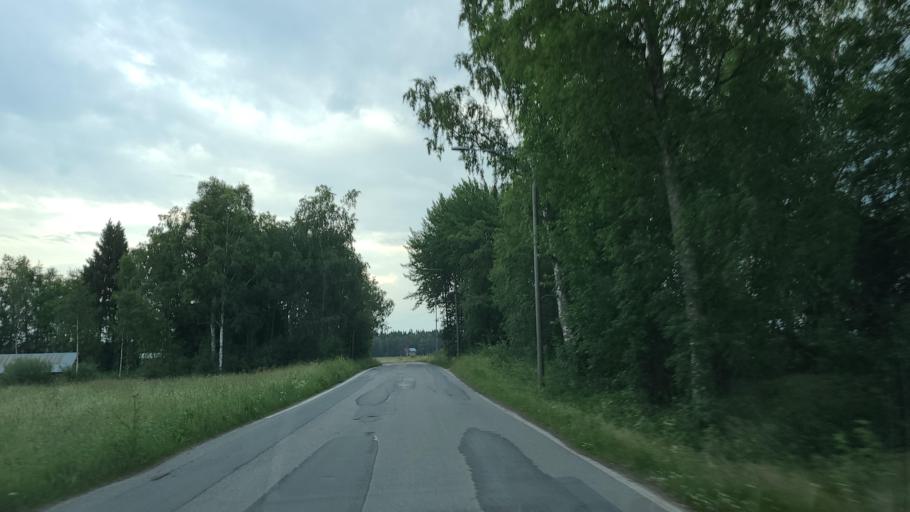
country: FI
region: Ostrobothnia
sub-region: Vaasa
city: Replot
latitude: 63.1840
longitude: 21.2923
